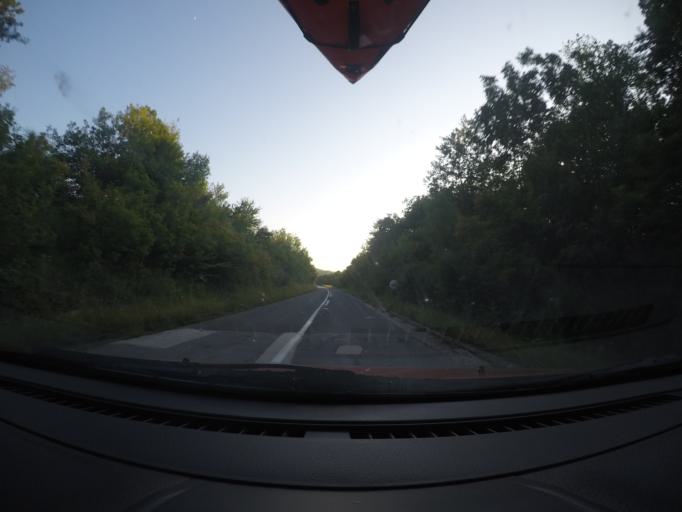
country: RO
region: Mehedinti
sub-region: Comuna Eselnita
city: Eselnita
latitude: 44.6715
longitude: 22.3806
